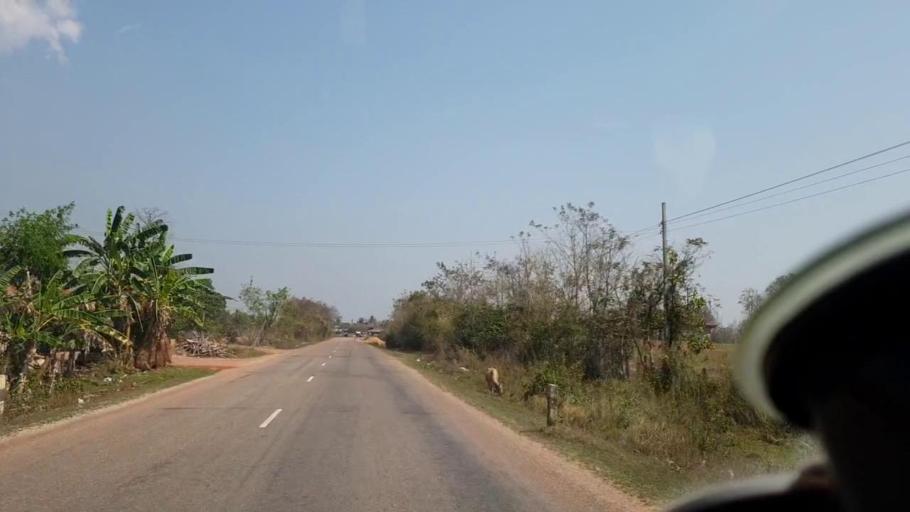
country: TH
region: Nong Khai
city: Rattanawapi
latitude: 18.2186
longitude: 103.0980
